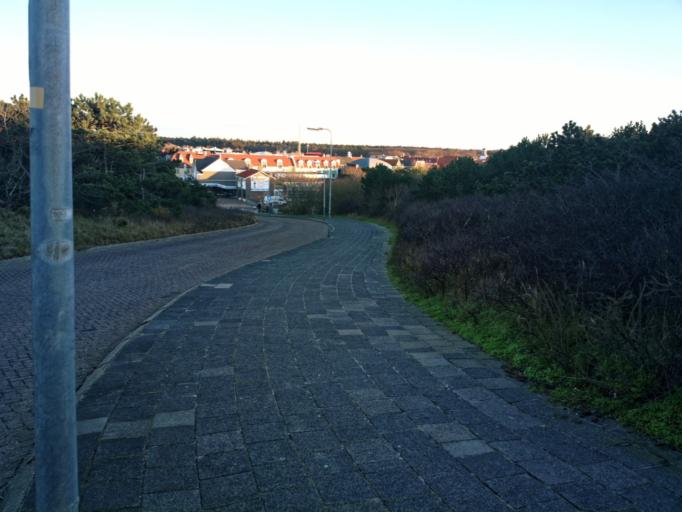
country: NL
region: North Holland
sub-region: Gemeente Texel
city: Den Burg
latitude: 53.1006
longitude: 4.7602
